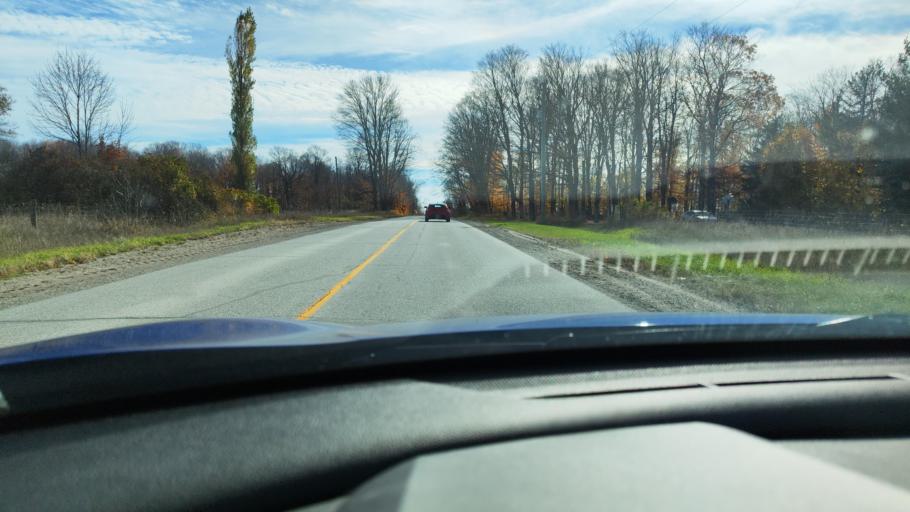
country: CA
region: Ontario
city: Wasaga Beach
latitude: 44.4572
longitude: -80.0026
